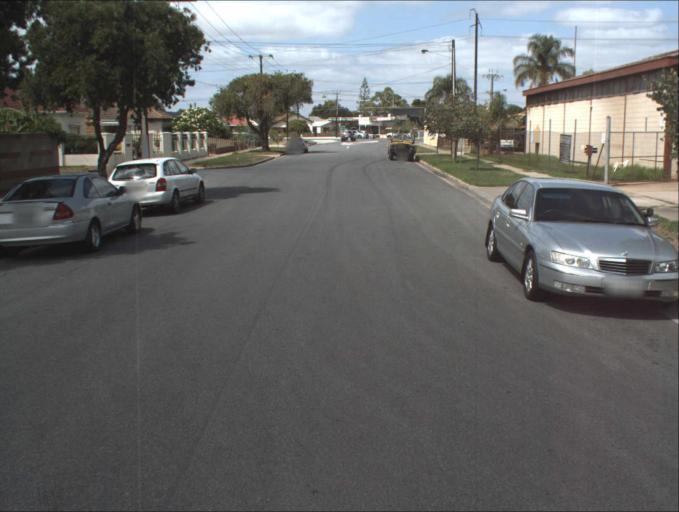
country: AU
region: South Australia
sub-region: Charles Sturt
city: Woodville
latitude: -34.8796
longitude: 138.5575
